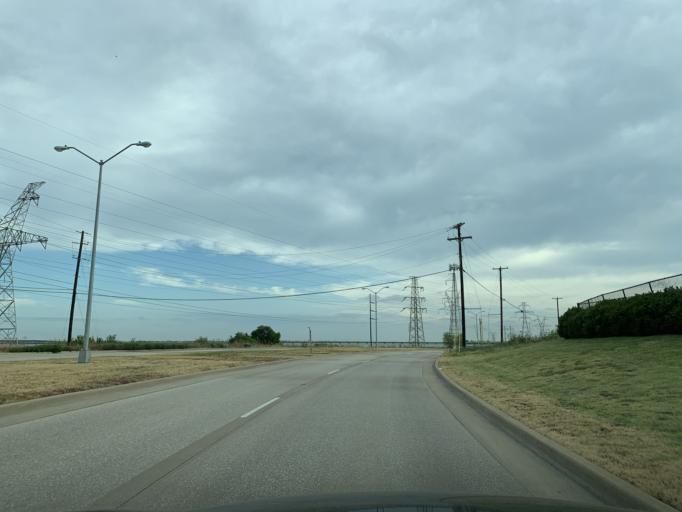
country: US
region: Texas
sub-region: Dallas County
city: Grand Prairie
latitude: 32.6963
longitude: -96.9630
